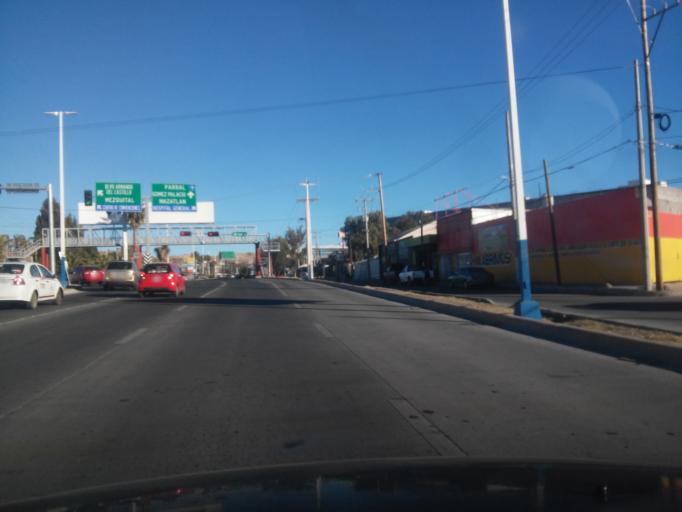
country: MX
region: Durango
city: Victoria de Durango
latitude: 24.0392
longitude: -104.6577
